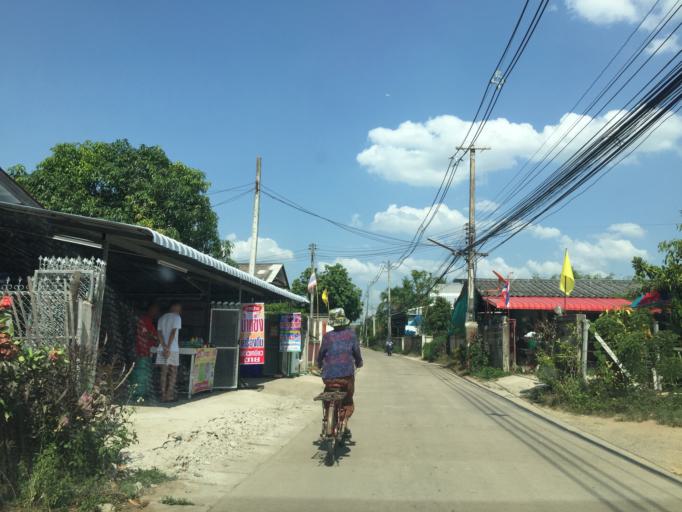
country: TH
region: Lamphun
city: Ban Thi
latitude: 18.6447
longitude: 99.0548
